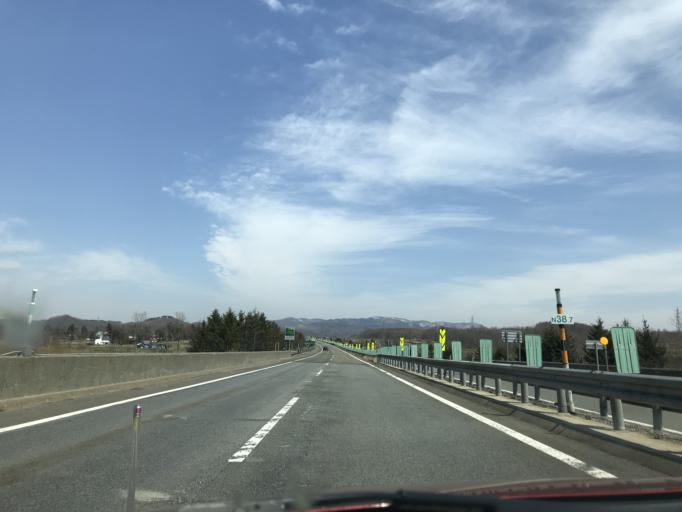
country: JP
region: Hokkaido
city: Iwamizawa
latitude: 43.2172
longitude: 141.8242
